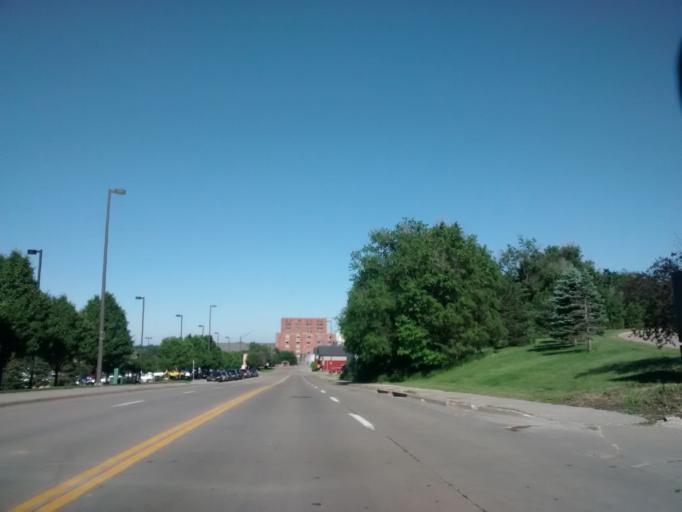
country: US
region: Nebraska
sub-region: Douglas County
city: Omaha
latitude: 41.2523
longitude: -95.9278
